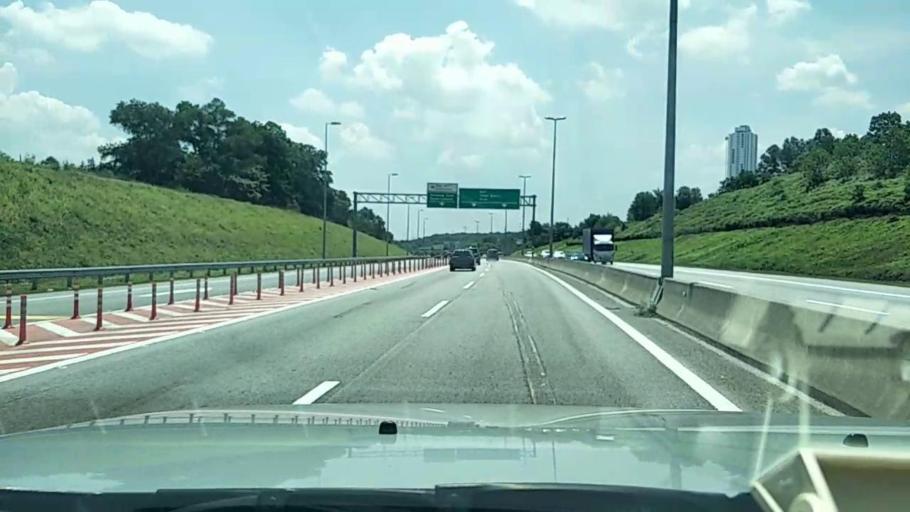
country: MY
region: Putrajaya
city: Putrajaya
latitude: 2.9376
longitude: 101.6561
